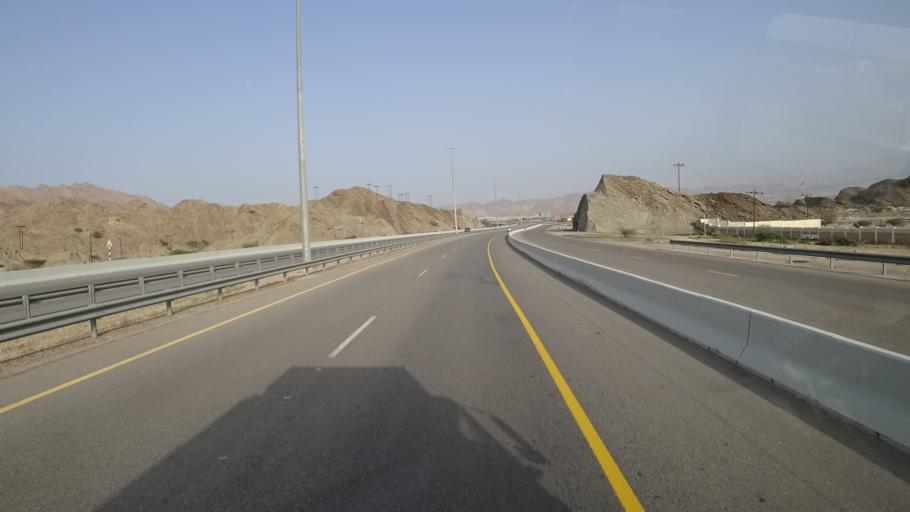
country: OM
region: Muhafazat Masqat
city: Muscat
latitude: 23.3423
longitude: 58.5831
